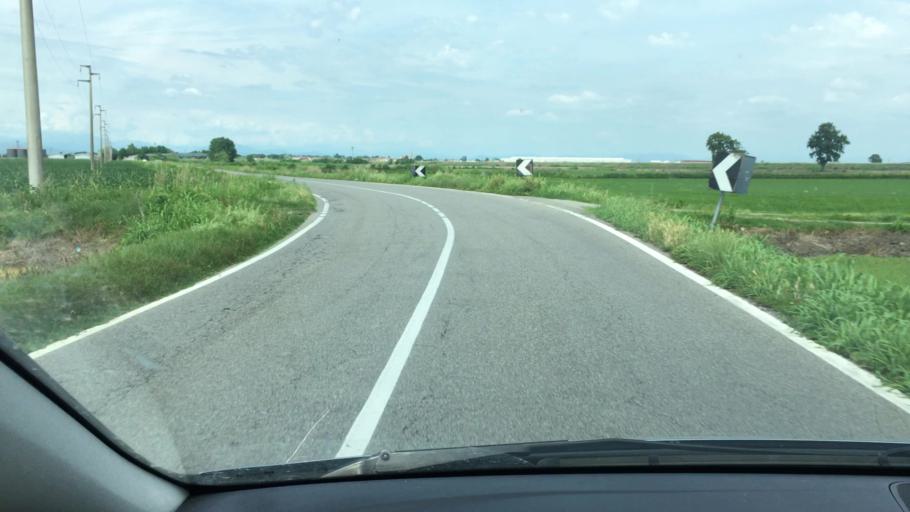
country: IT
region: Piedmont
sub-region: Provincia di Novara
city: Casalvolone
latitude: 45.4174
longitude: 8.4643
